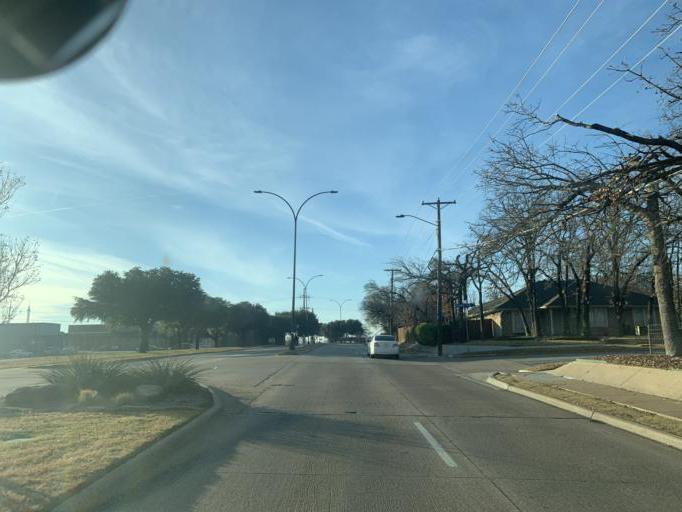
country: US
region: Texas
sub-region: Tarrant County
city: Arlington
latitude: 32.7666
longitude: -97.0738
